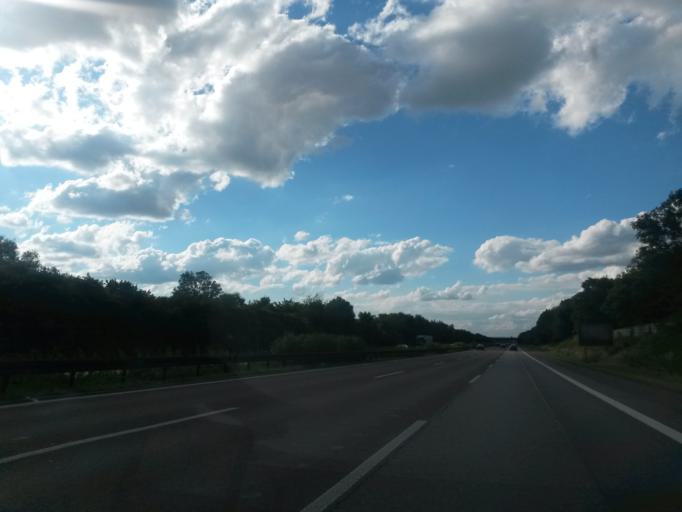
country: DE
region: Bavaria
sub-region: Upper Bavaria
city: Manching
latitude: 48.7322
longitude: 11.4714
